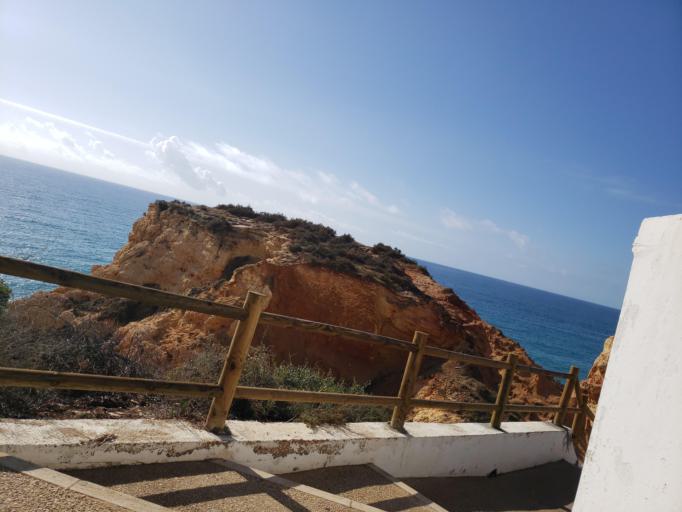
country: PT
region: Faro
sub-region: Lagoa
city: Carvoeiro
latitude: 37.0931
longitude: -8.4652
